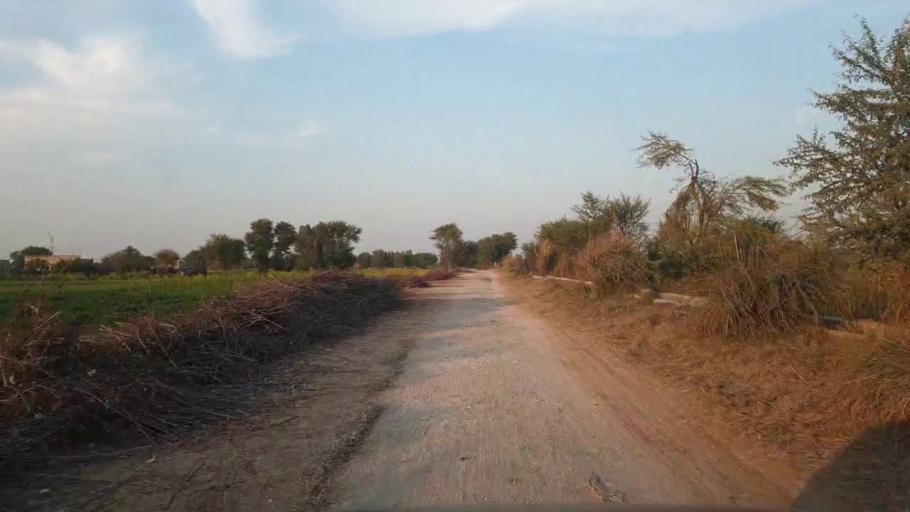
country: PK
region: Sindh
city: Shahpur Chakar
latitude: 26.1960
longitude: 68.6182
